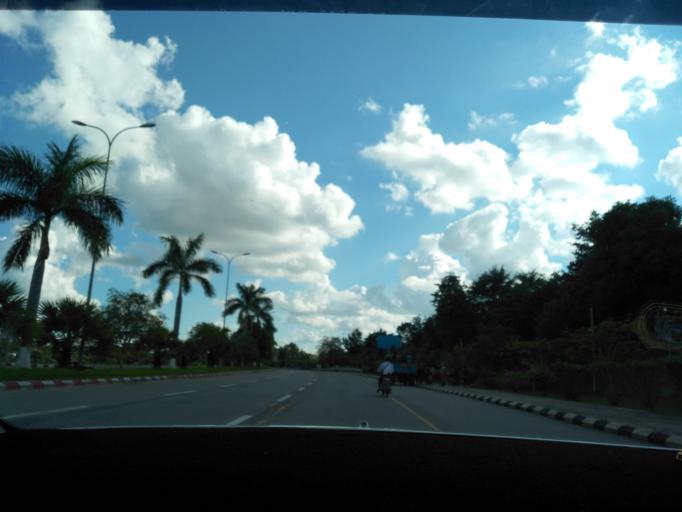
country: MM
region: Mandalay
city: Nay Pyi Taw
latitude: 19.7347
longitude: 96.1117
